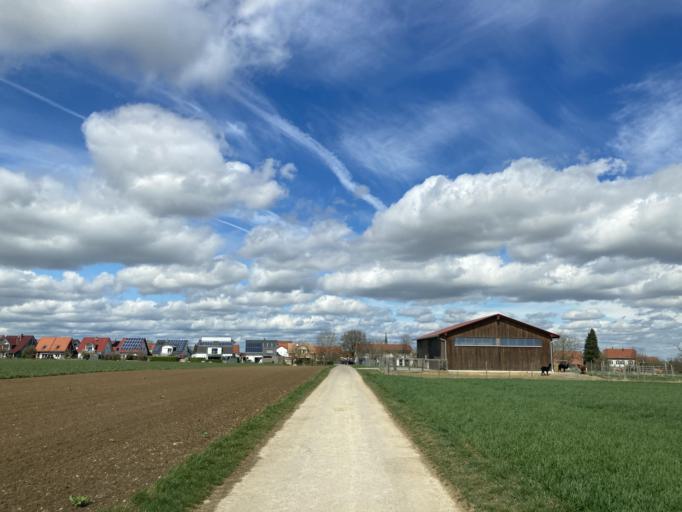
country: DE
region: Baden-Wuerttemberg
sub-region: Regierungsbezirk Stuttgart
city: Bondorf
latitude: 48.4687
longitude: 8.8190
